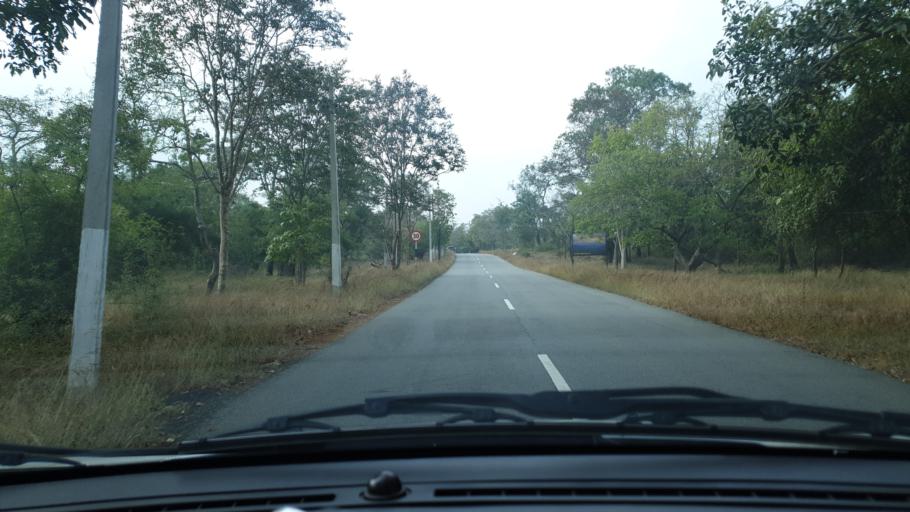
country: IN
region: Andhra Pradesh
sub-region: Kurnool
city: Srisailam
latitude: 16.2818
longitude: 78.7262
